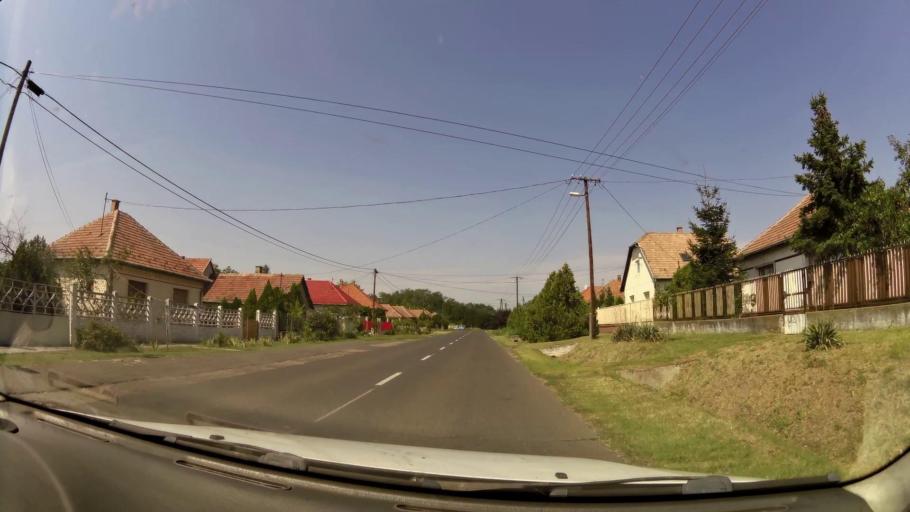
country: HU
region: Pest
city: Tapiosag
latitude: 47.4072
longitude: 19.6179
